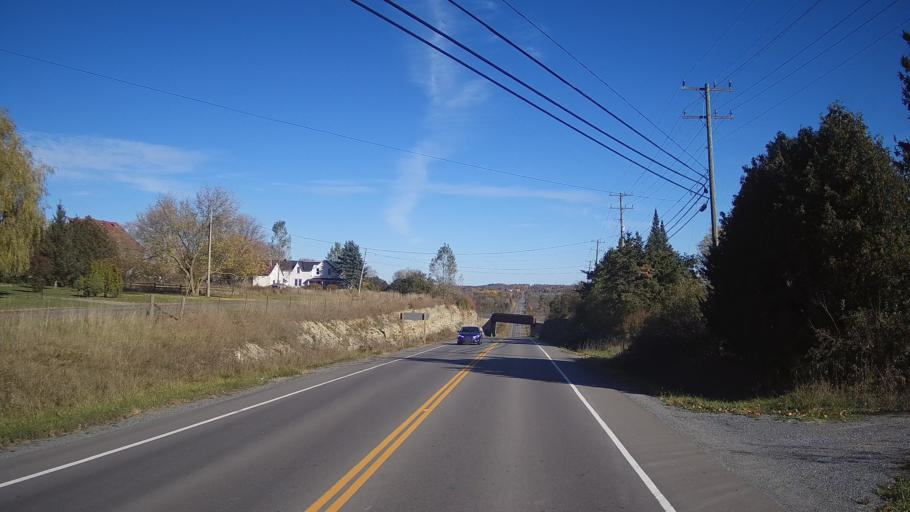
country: CA
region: Ontario
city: Kingston
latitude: 44.4054
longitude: -76.6386
